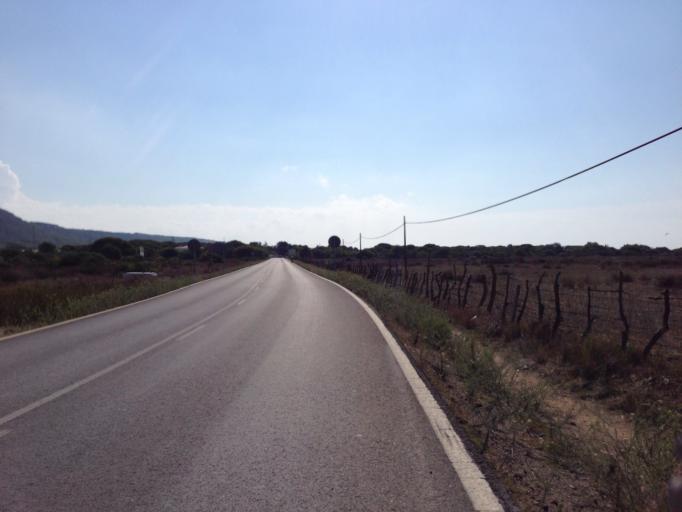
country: ES
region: Andalusia
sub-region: Provincia de Cadiz
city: Vejer de la Frontera
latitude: 36.1921
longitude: -6.0307
